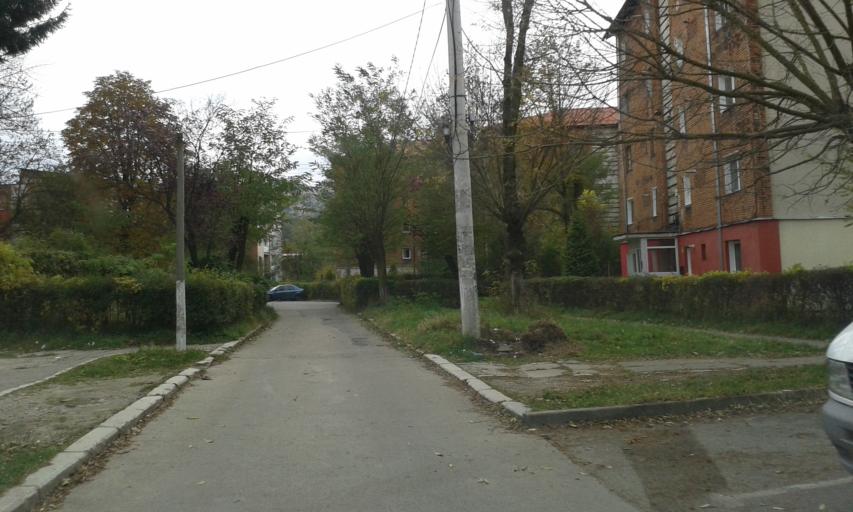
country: RO
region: Hunedoara
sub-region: Municipiul Petrosani
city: Petrosani
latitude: 45.3978
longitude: 23.3771
